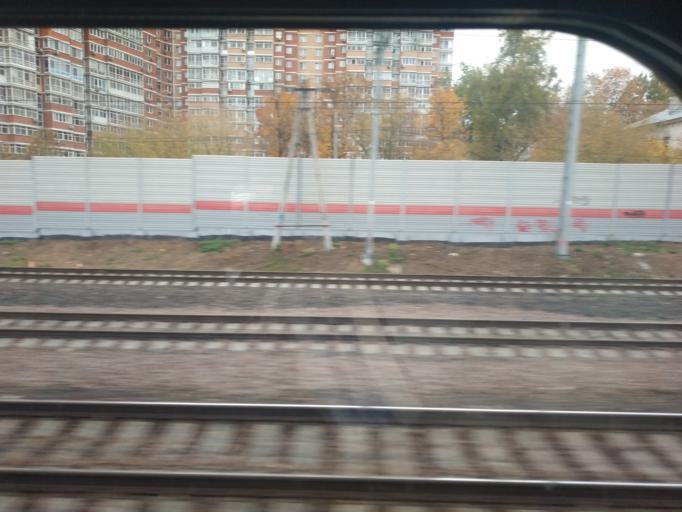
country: RU
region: Moskovskaya
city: Odintsovo
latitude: 55.6767
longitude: 37.2919
